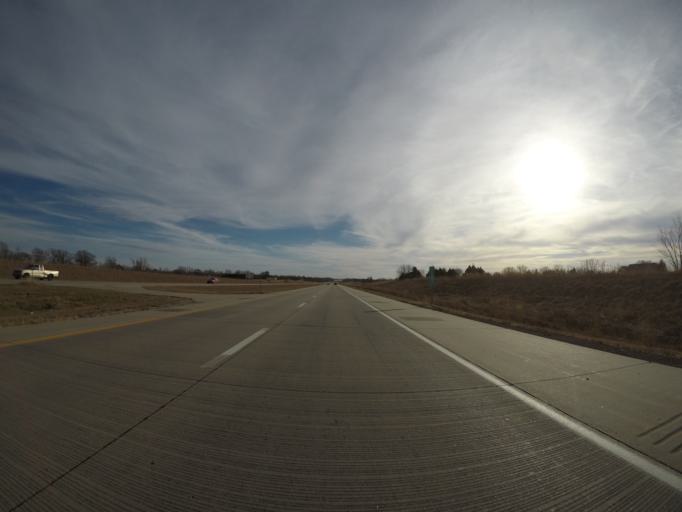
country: US
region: Kansas
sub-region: Franklin County
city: Ottawa
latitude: 38.6170
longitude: -95.2326
